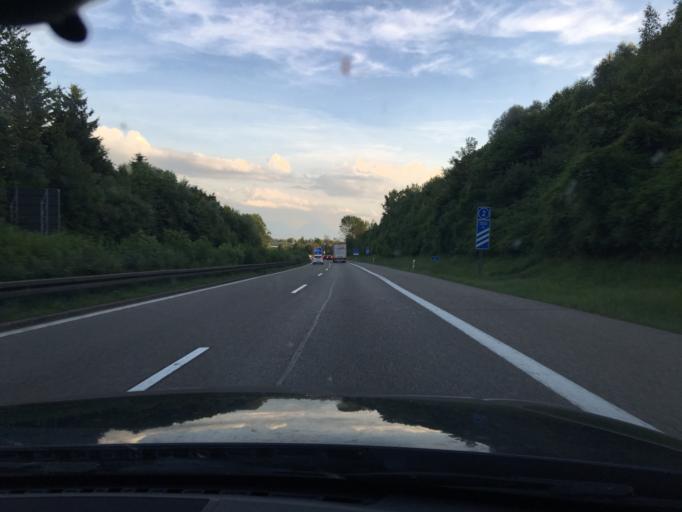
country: AT
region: Vorarlberg
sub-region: Politischer Bezirk Bregenz
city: Horbranz
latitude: 47.5565
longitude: 9.7348
